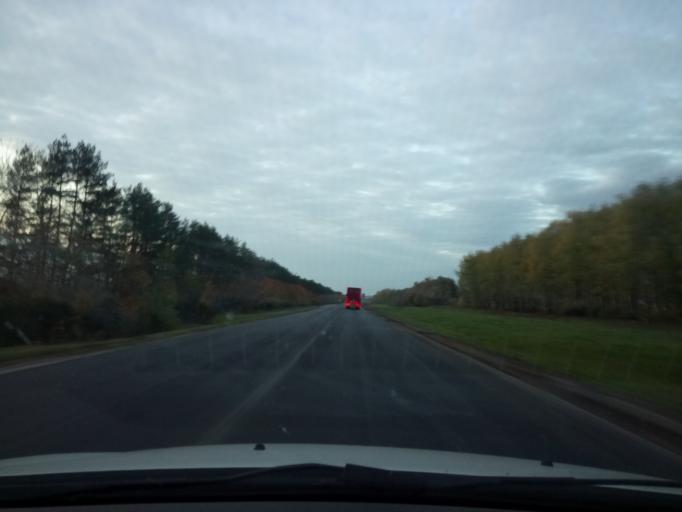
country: RU
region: Nizjnij Novgorod
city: Bol'shoye Murashkino
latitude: 55.8213
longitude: 44.7572
